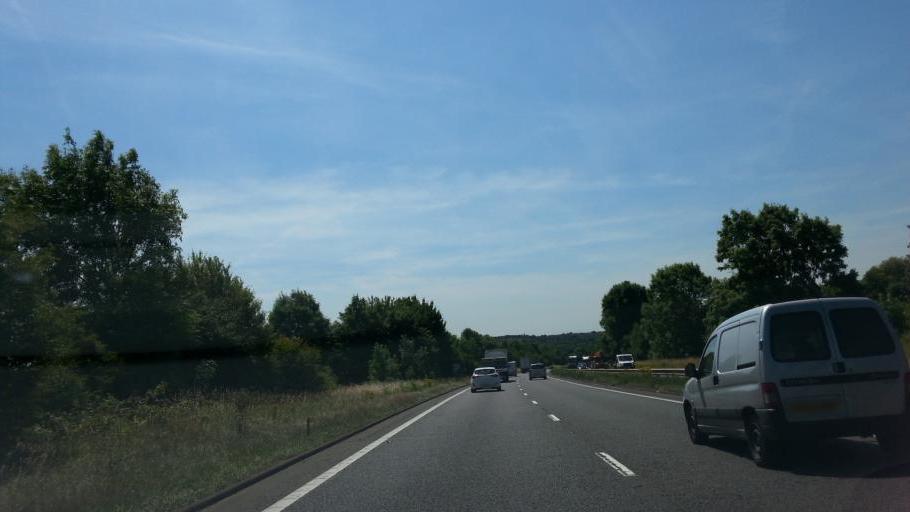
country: GB
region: England
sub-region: Derbyshire
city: Alfreton
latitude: 53.0685
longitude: -1.4084
